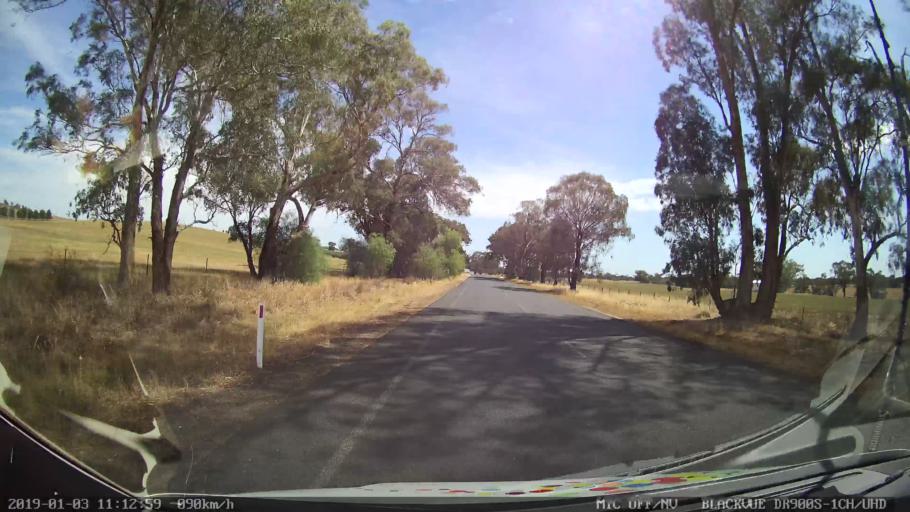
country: AU
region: New South Wales
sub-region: Young
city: Young
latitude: -34.1947
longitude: 148.2617
